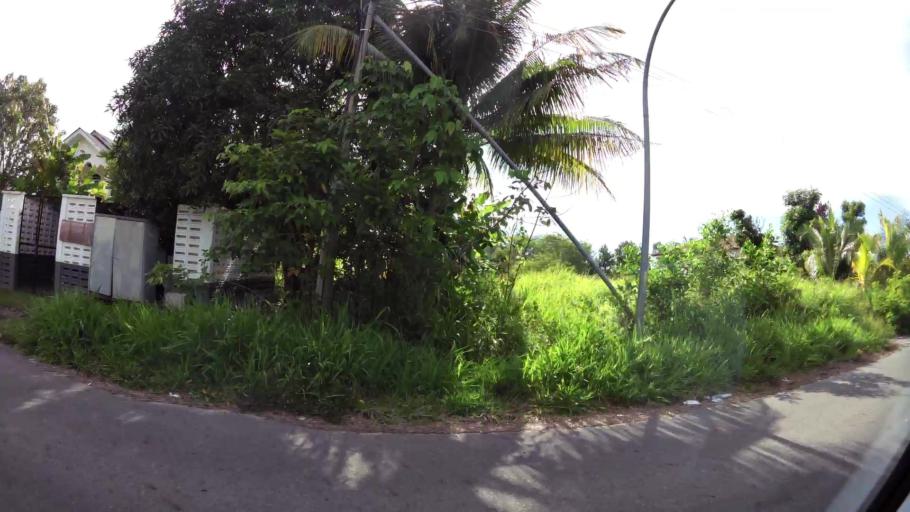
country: BN
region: Brunei and Muara
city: Bandar Seri Begawan
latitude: 4.9680
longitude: 115.0236
